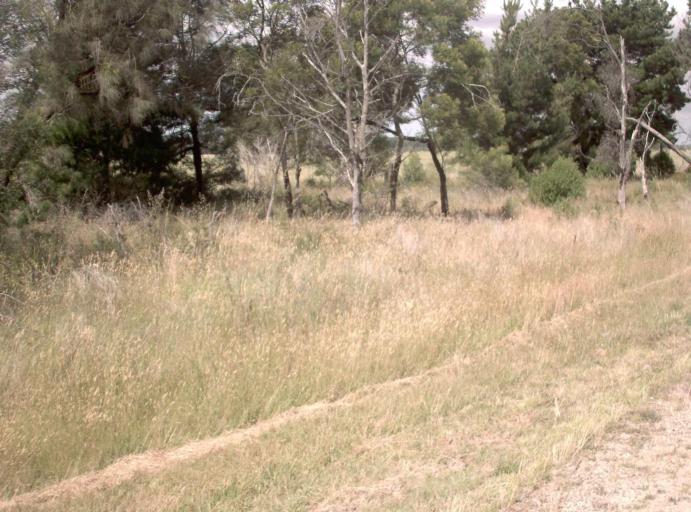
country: AU
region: Victoria
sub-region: Wellington
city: Sale
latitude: -38.1694
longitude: 146.9628
